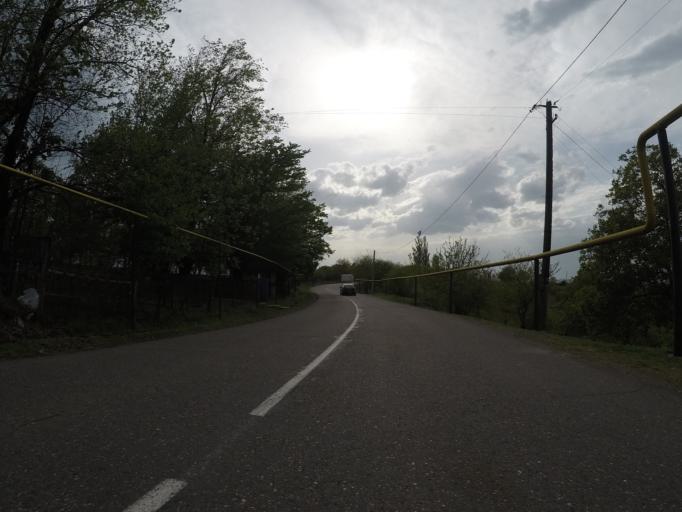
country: GE
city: Shorapani
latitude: 42.1465
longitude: 43.1007
